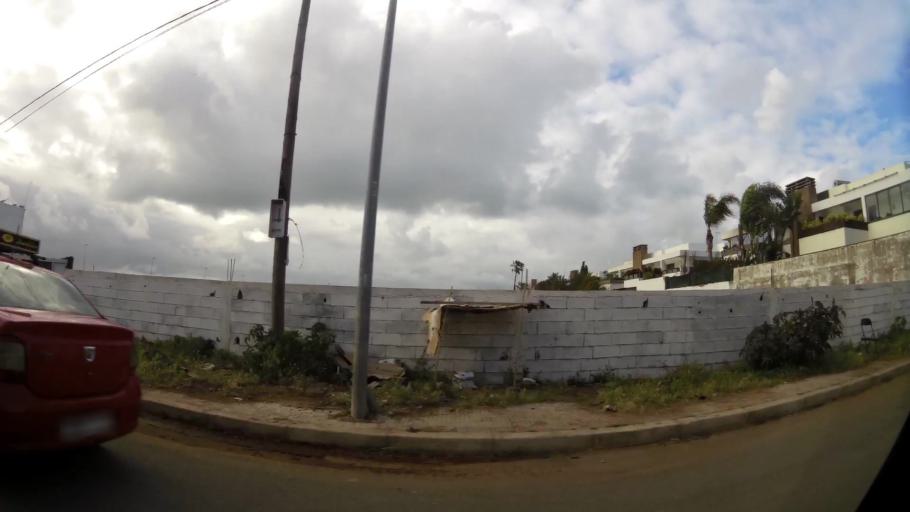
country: MA
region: Grand Casablanca
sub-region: Casablanca
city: Casablanca
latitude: 33.5776
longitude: -7.6973
